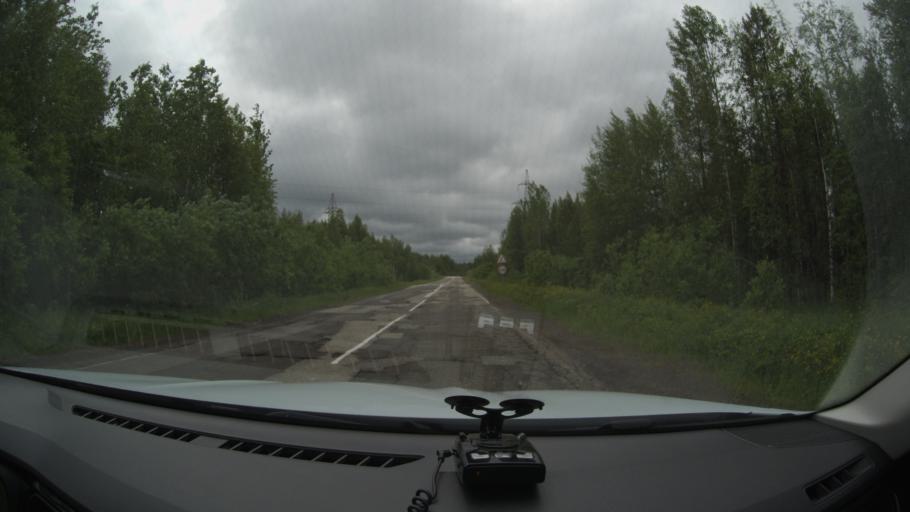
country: RU
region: Komi Republic
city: Nizhniy Odes
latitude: 63.6349
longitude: 54.6361
